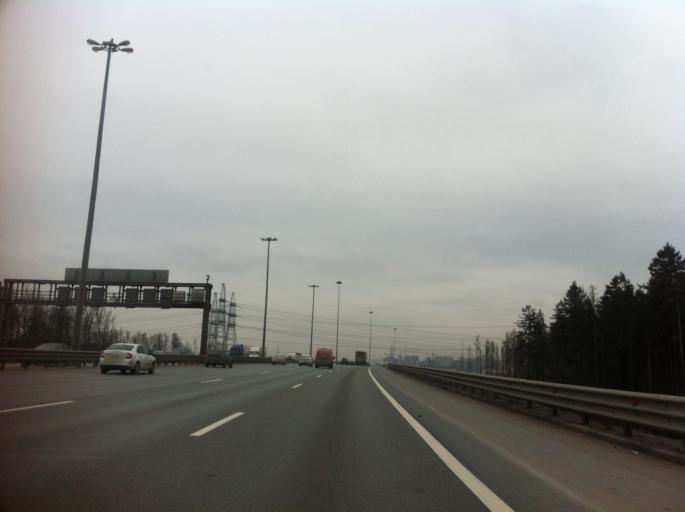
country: RU
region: St.-Petersburg
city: Krasnogvargeisky
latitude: 59.9336
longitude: 30.5376
